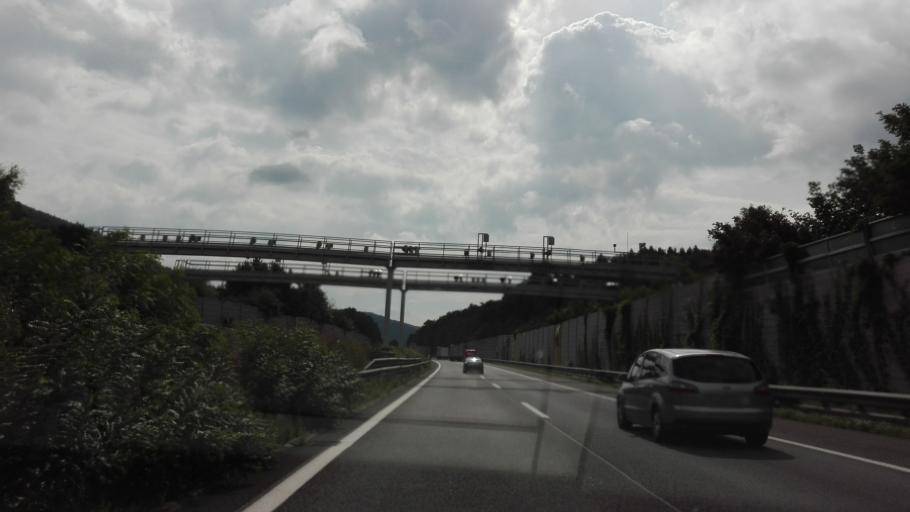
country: AT
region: Lower Austria
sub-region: Politischer Bezirk Baden
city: Klausen-Leopoldsdorf
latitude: 48.0880
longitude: 16.0094
